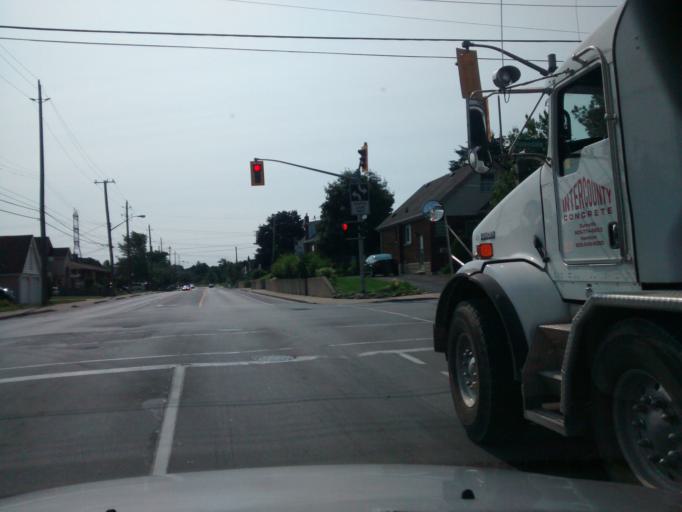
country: CA
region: Ontario
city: Hamilton
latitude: 43.2302
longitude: -79.8086
